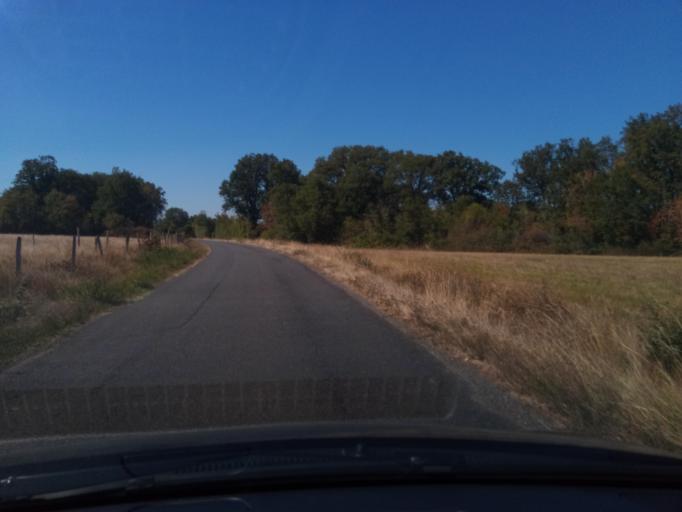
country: FR
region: Poitou-Charentes
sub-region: Departement de la Vienne
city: Montmorillon
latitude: 46.4817
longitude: 0.8854
